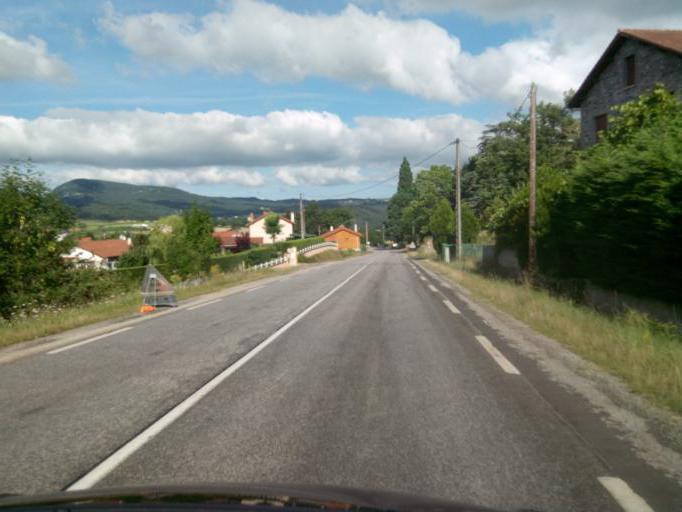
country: FR
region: Auvergne
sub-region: Departement de la Haute-Loire
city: Retournac
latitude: 45.2252
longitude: 4.0385
